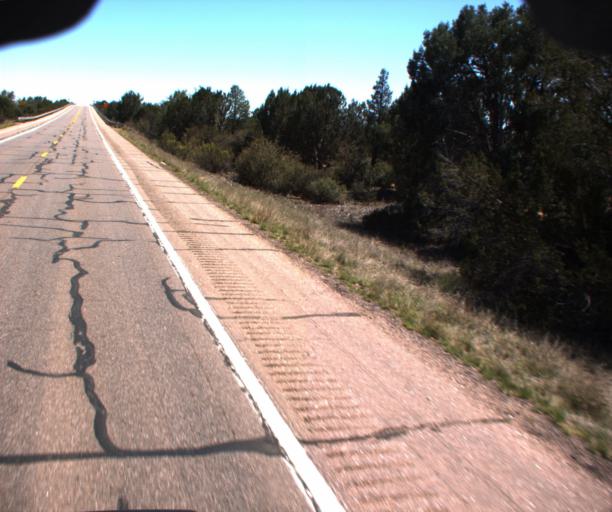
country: US
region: Arizona
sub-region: Yavapai County
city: Paulden
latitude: 35.0160
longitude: -112.3918
